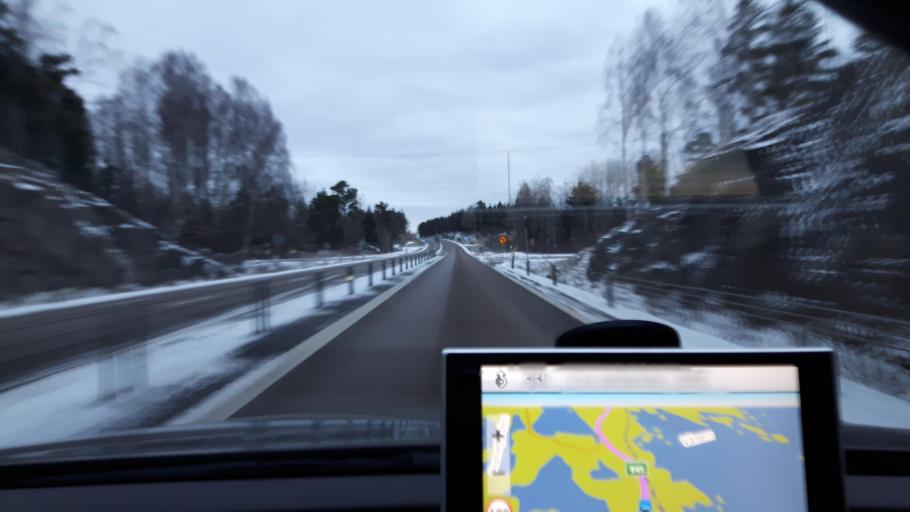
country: SE
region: Vaestra Goetaland
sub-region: Melleruds Kommun
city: Mellerud
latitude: 58.7950
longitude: 12.5205
